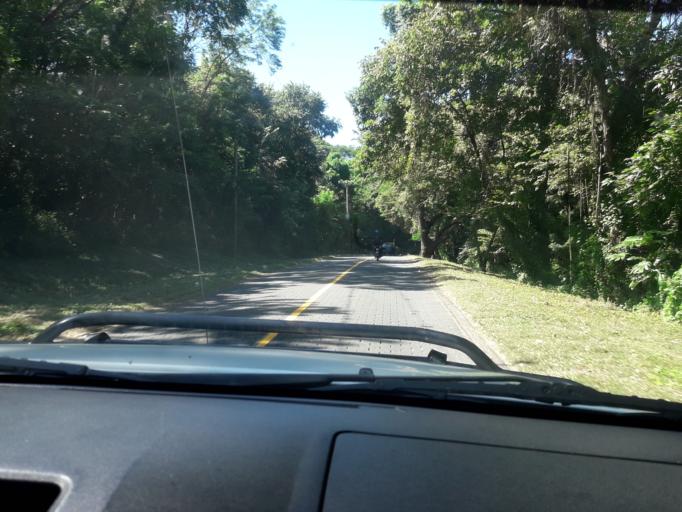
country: NI
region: Rivas
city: Cardenas
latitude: 11.2310
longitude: -85.5479
